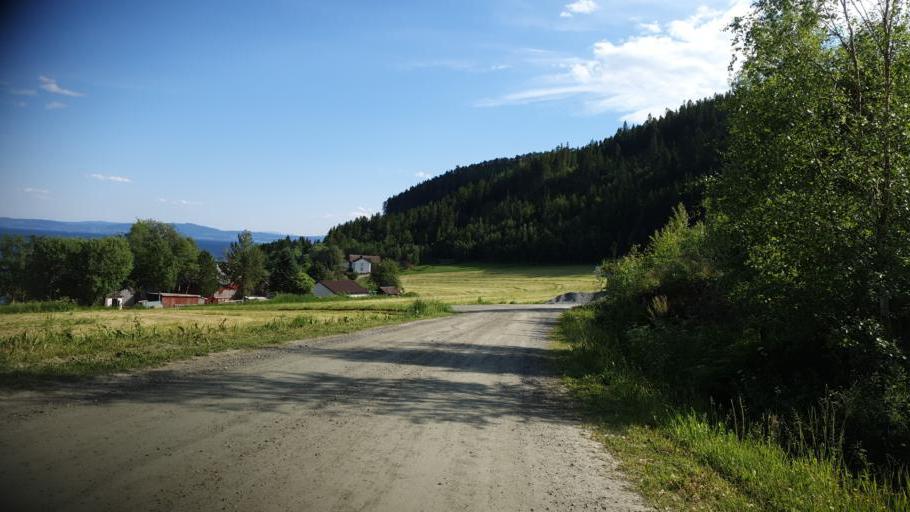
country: NO
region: Sor-Trondelag
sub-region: Trondheim
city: Trondheim
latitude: 63.5831
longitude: 10.4146
